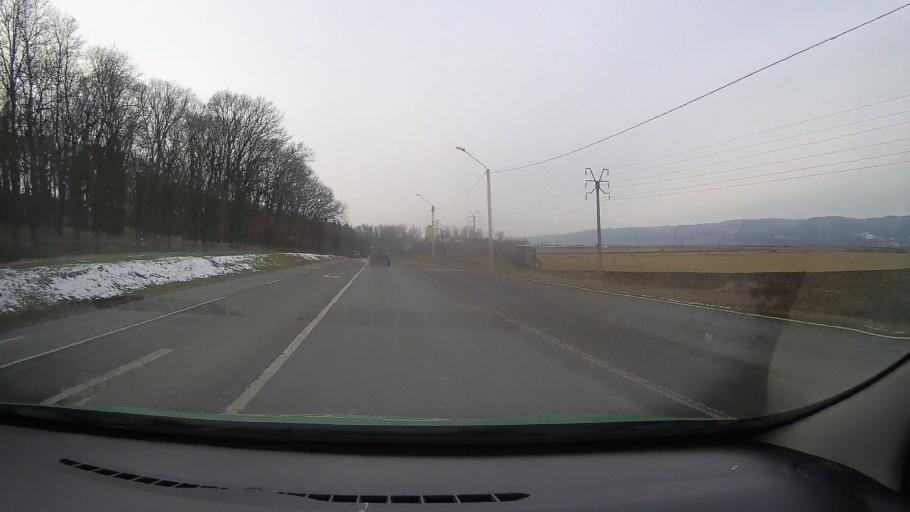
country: RO
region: Hunedoara
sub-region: Comuna Turdas
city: Pricaz
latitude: 45.8386
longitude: 23.1780
